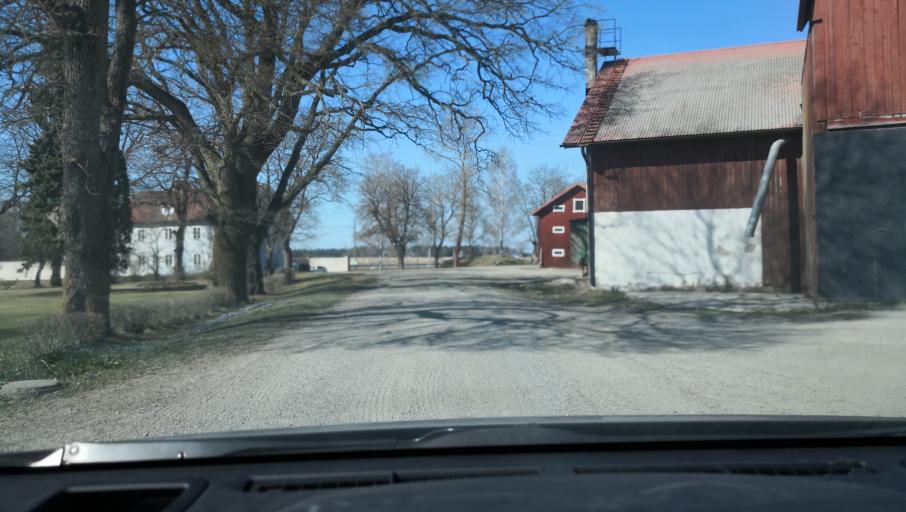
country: SE
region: Vaestmanland
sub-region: Sala Kommun
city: Sala
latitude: 59.8564
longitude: 16.5389
